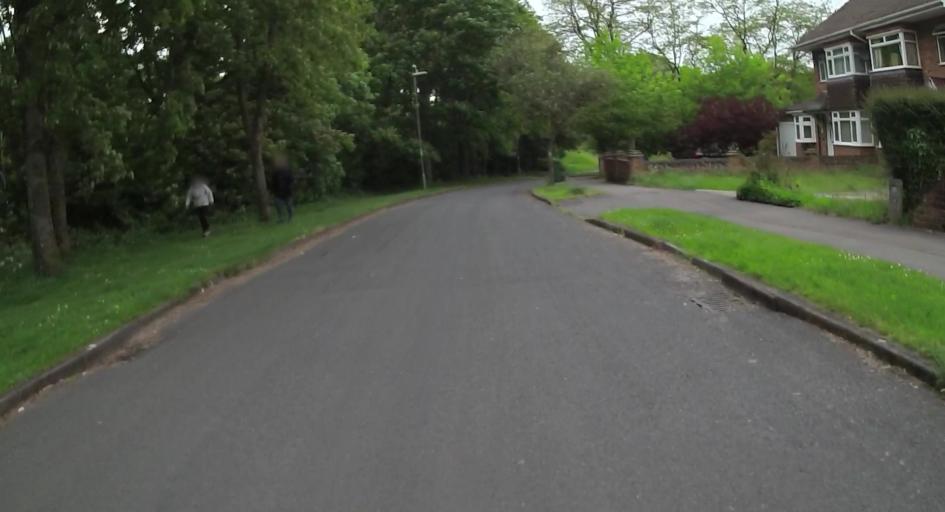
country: GB
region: England
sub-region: Hampshire
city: Basingstoke
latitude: 51.2488
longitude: -1.0957
